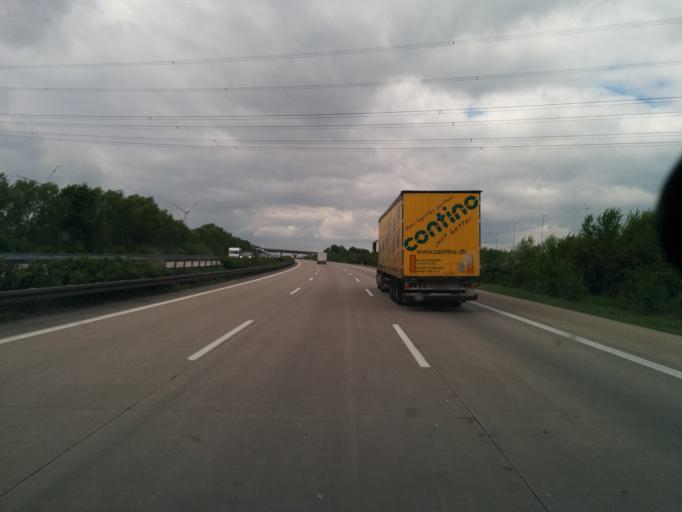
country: DE
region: Saxony-Anhalt
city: Irxleben
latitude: 52.1757
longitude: 11.4823
